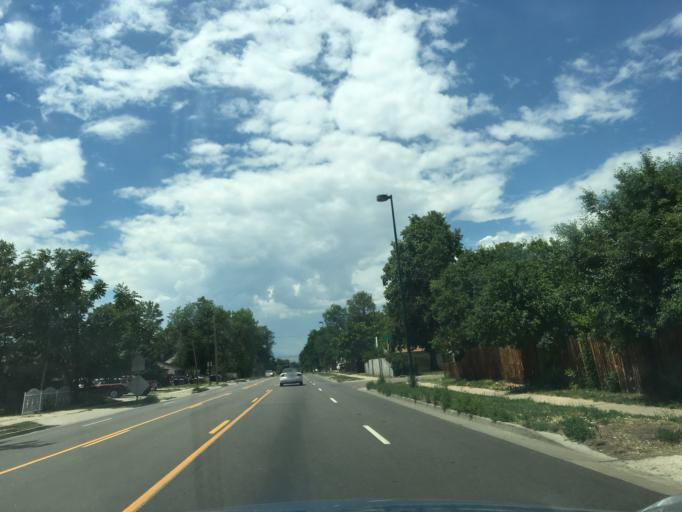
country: US
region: Colorado
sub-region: Arapahoe County
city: Sheridan
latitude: 39.6968
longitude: -105.0163
